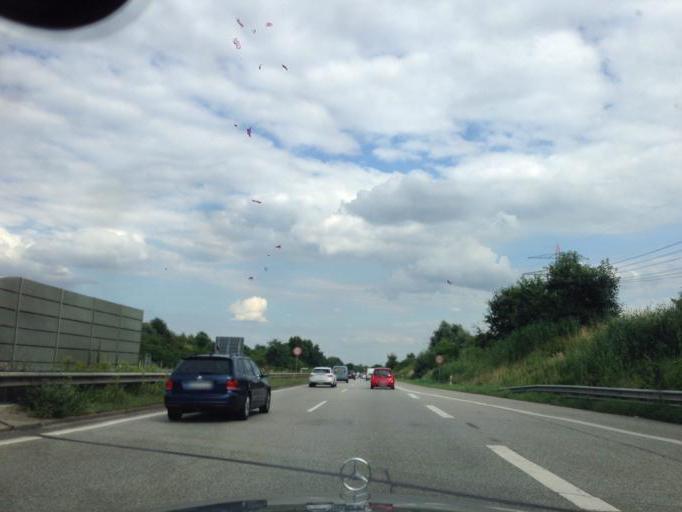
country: DE
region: Schleswig-Holstein
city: Oststeinbek
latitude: 53.4852
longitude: 10.1225
